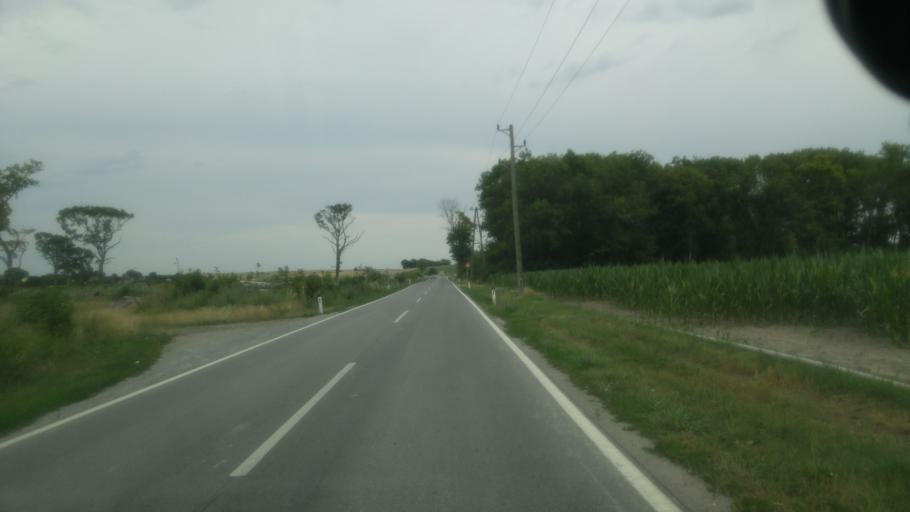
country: AT
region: Lower Austria
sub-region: Politischer Bezirk Wien-Umgebung
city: Moosbrunn
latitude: 48.0369
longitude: 16.4341
